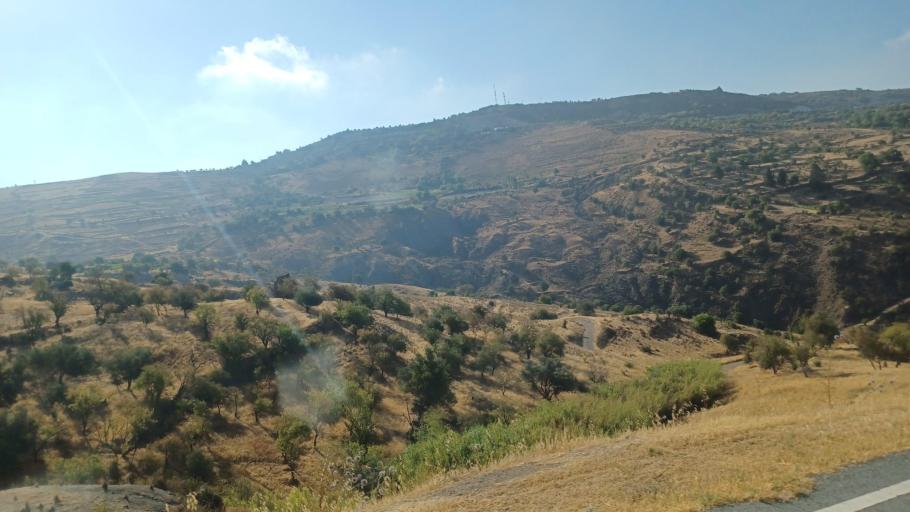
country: CY
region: Pafos
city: Mesogi
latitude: 34.8703
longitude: 32.6092
